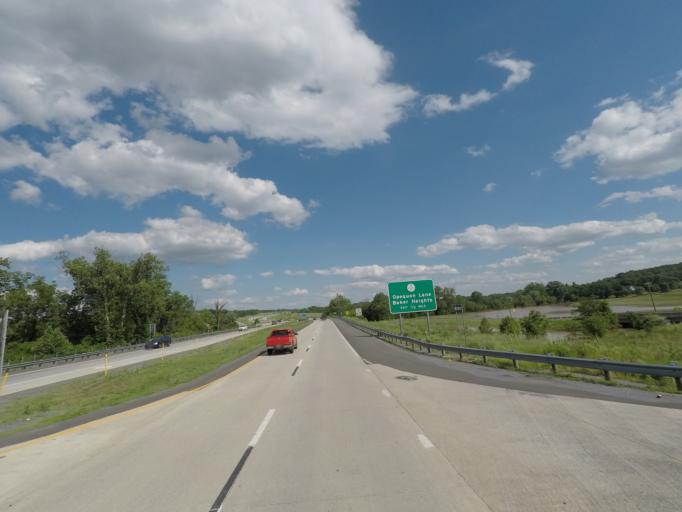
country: US
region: West Virginia
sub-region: Berkeley County
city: Martinsburg
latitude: 39.4262
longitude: -77.9404
